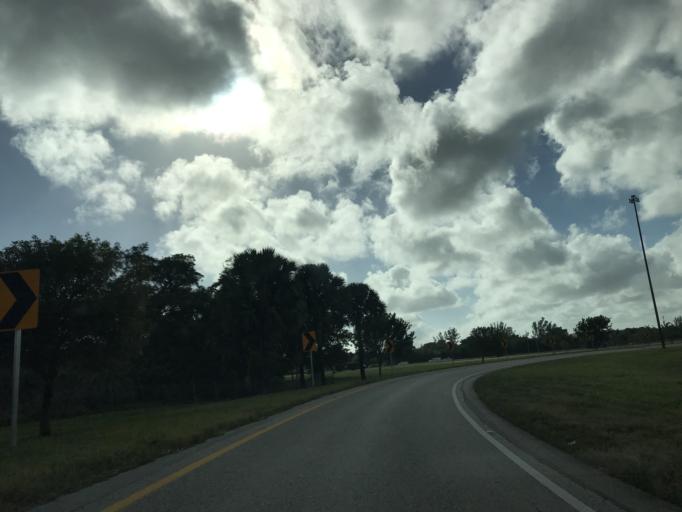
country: US
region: Florida
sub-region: Palm Beach County
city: Boca Pointe
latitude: 26.3081
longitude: -80.1662
